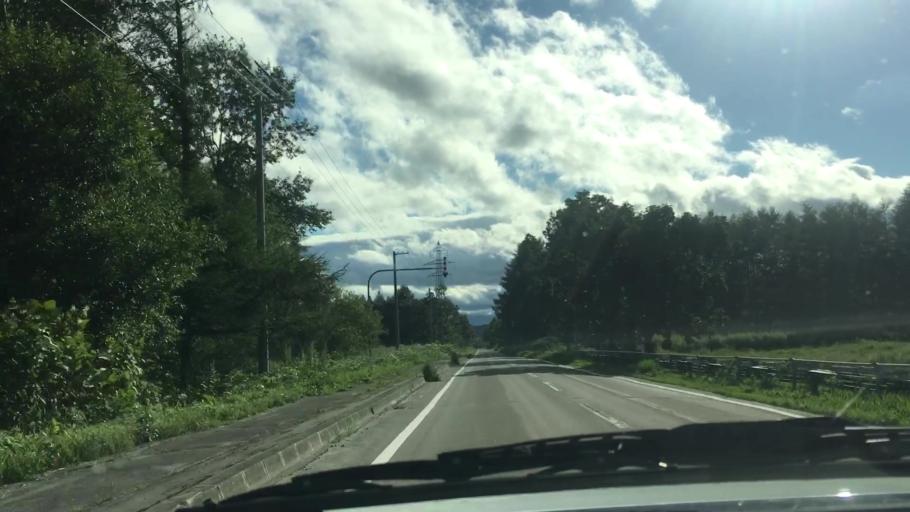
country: JP
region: Hokkaido
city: Otofuke
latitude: 43.1823
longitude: 143.0154
